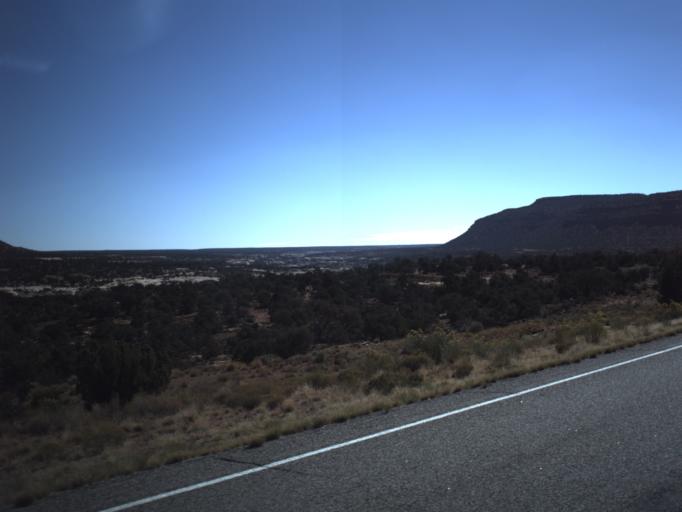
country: US
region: Utah
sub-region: San Juan County
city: Blanding
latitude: 37.6246
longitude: -110.0860
